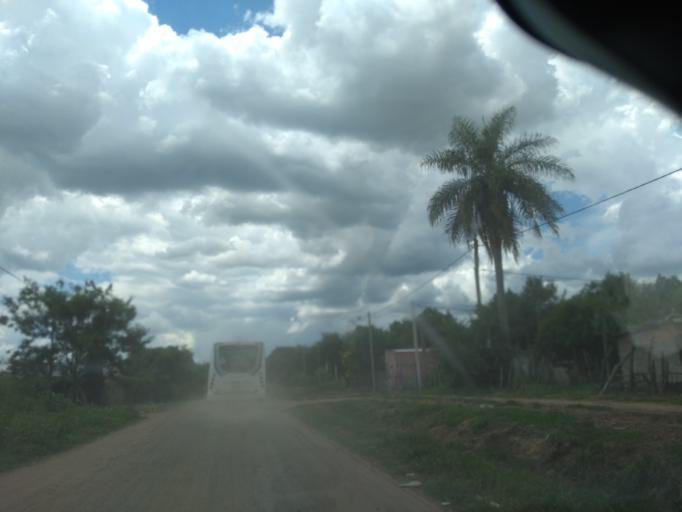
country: AR
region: Chaco
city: Fontana
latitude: -27.4037
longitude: -59.0427
